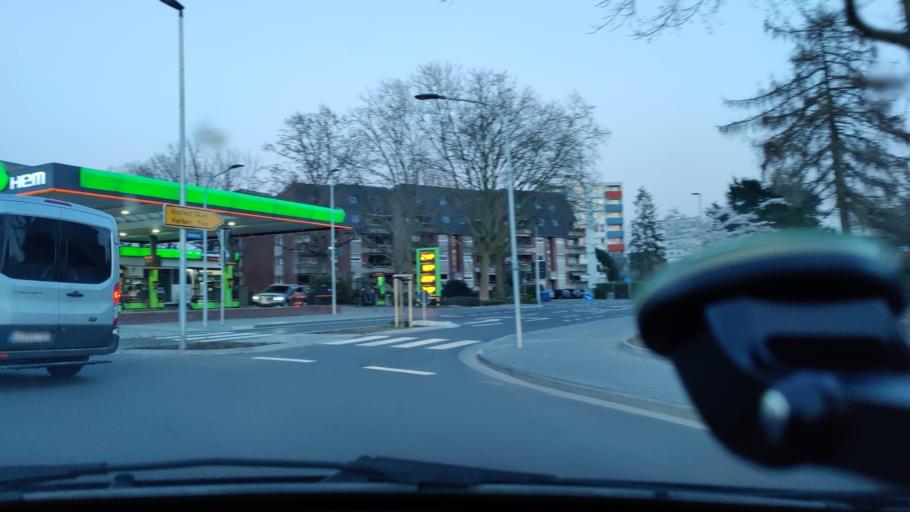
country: DE
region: North Rhine-Westphalia
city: Geldern
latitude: 51.5149
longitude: 6.3271
